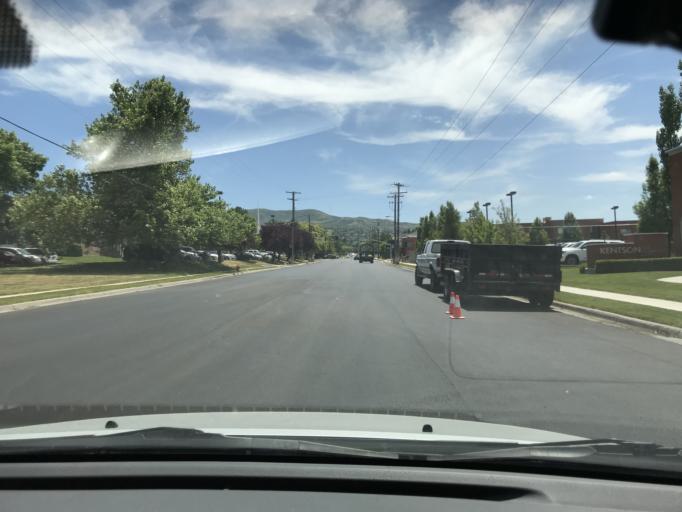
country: US
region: Utah
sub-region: Davis County
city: Woods Cross
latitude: 40.8630
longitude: -111.8923
